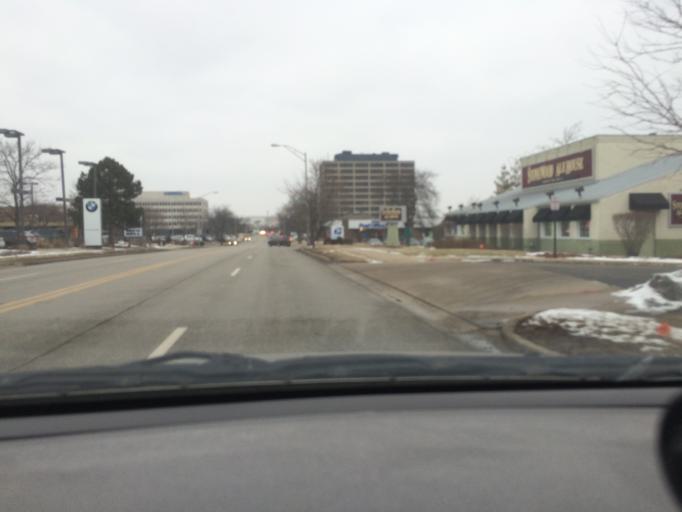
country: US
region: Illinois
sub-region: Cook County
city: Hoffman Estates
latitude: 42.0396
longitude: -88.0389
